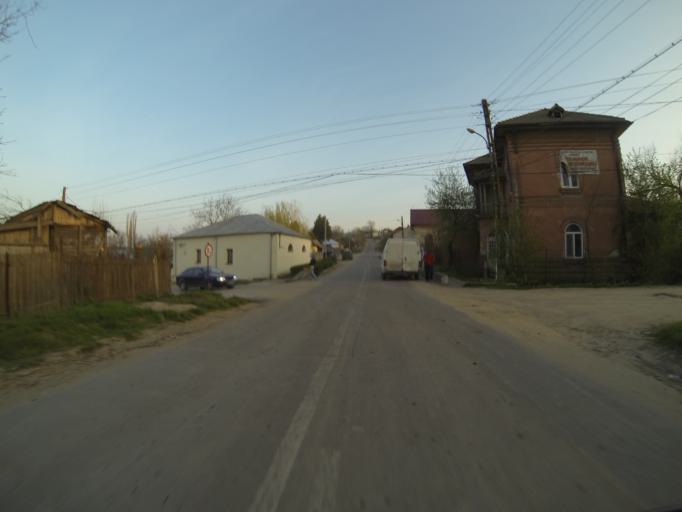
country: RO
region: Dolj
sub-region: Comuna Dranicu
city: Dranic
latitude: 44.0551
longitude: 23.8456
